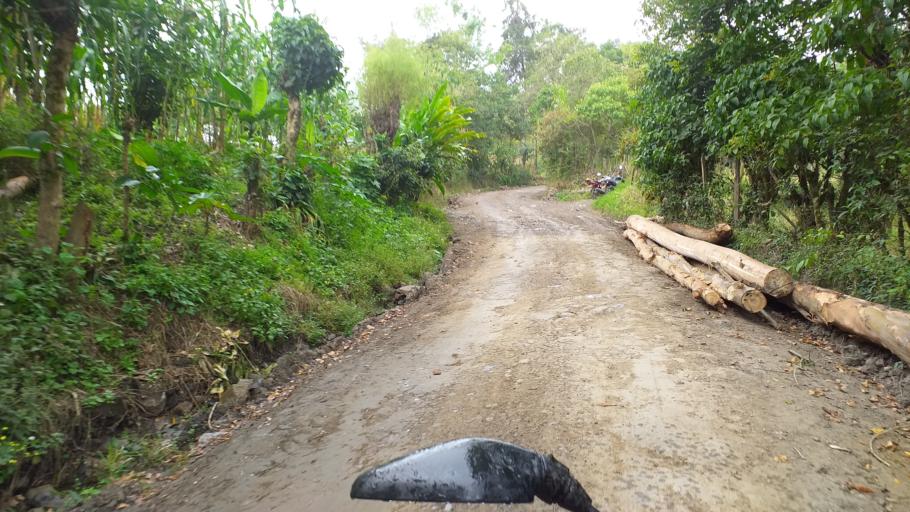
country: CO
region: Cundinamarca
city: Tenza
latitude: 5.0921
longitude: -73.4528
